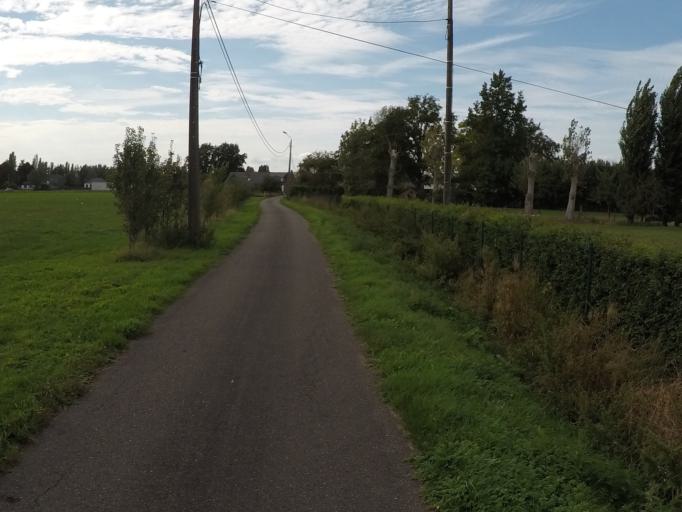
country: BE
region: Flanders
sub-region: Provincie Antwerpen
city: Lier
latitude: 51.1021
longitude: 4.5895
